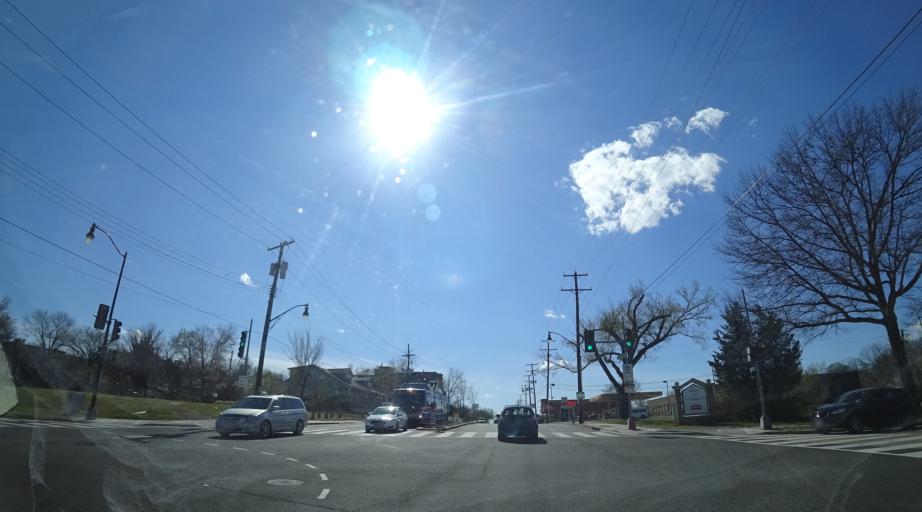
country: US
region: Maryland
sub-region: Prince George's County
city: Cottage City
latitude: 38.9309
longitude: -76.9577
